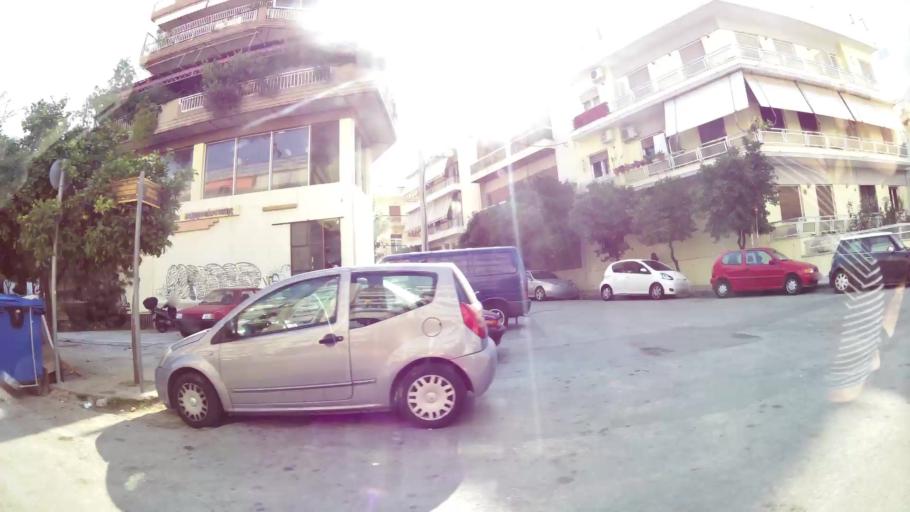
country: GR
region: Attica
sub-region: Nomarchia Athinas
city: Palaio Faliro
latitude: 37.9345
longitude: 23.7099
